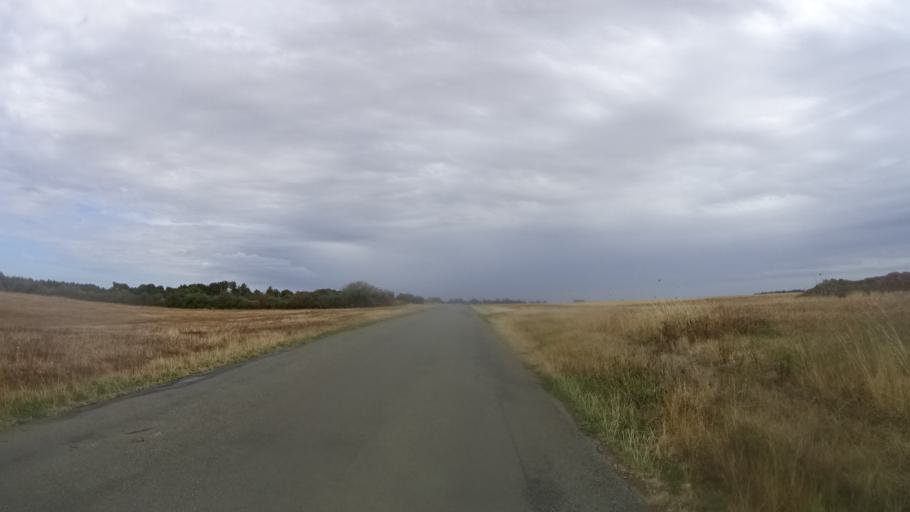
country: FR
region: Centre
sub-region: Departement du Loiret
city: Boynes
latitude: 48.1939
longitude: 2.3954
